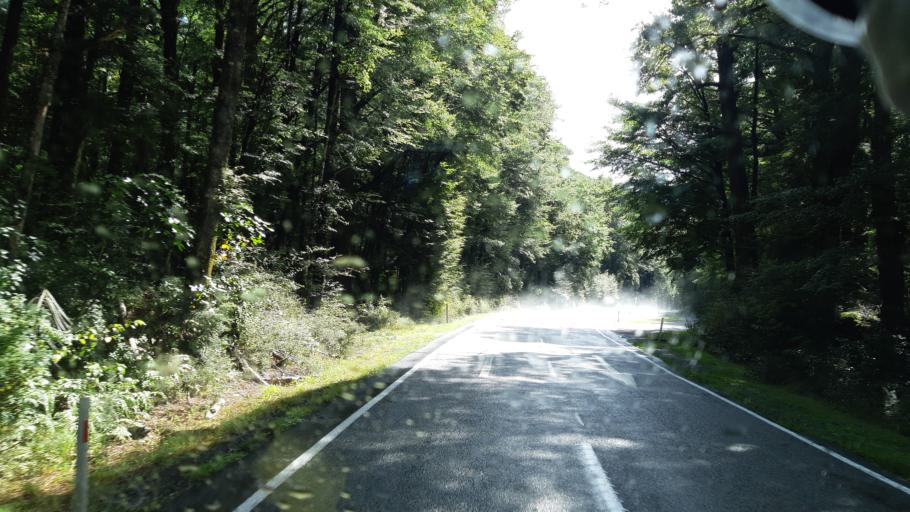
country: NZ
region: Canterbury
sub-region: Hurunui District
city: Amberley
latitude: -42.3791
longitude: 172.2784
